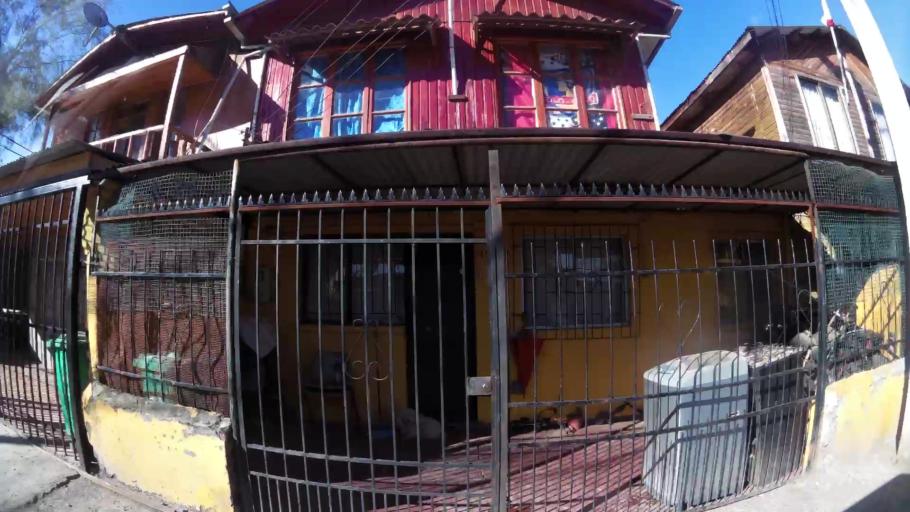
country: CL
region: Santiago Metropolitan
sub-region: Provincia de Maipo
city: San Bernardo
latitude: -33.6027
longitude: -70.6831
